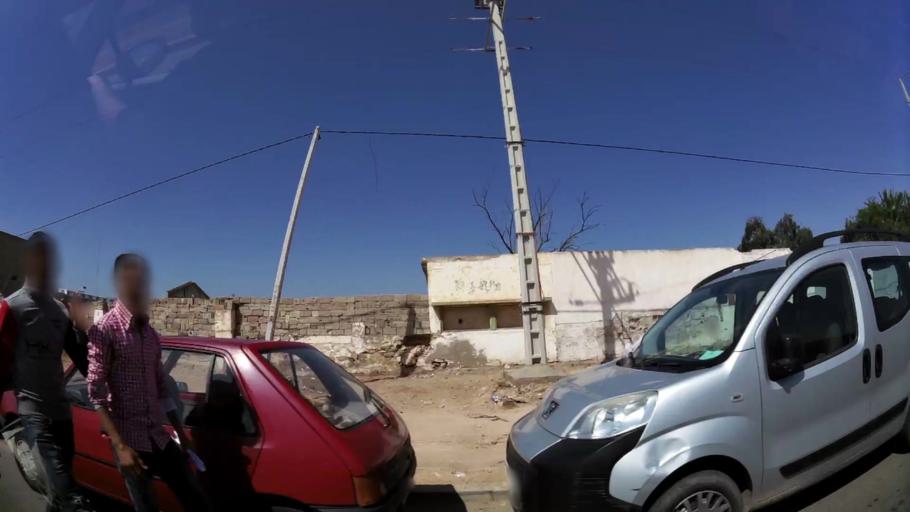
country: MA
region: Souss-Massa-Draa
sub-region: Agadir-Ida-ou-Tnan
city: Agadir
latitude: 30.4203
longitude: -9.5802
